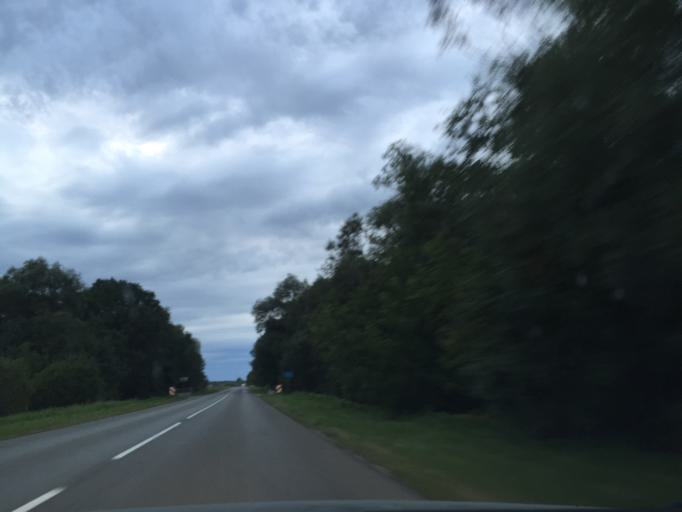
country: LV
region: Vecumnieki
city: Vecumnieki
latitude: 56.5161
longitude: 24.5600
